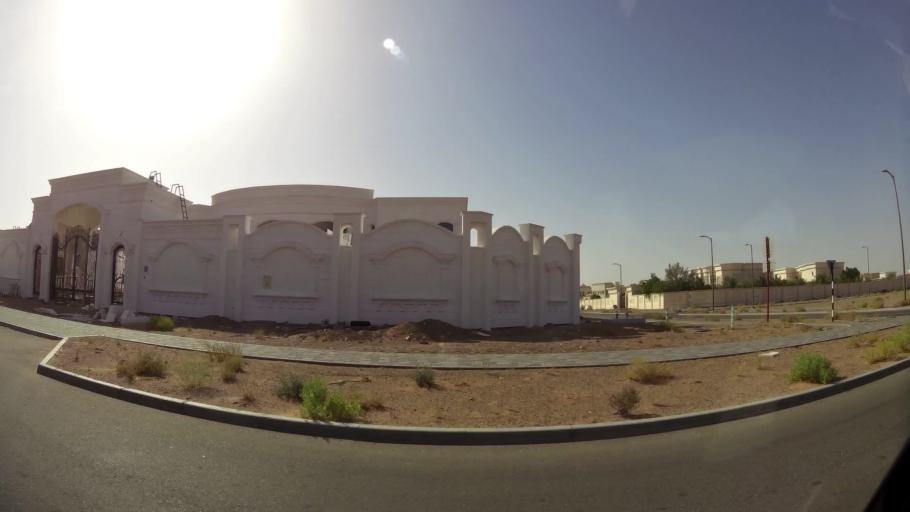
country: OM
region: Al Buraimi
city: Al Buraymi
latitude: 24.3601
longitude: 55.7889
